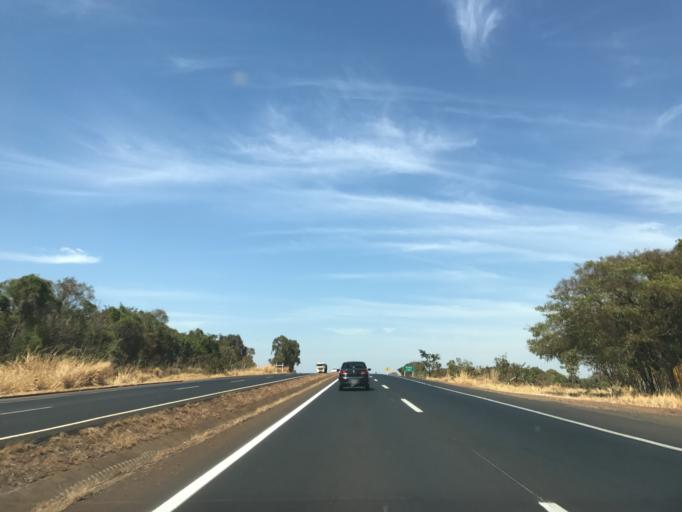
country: BR
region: Minas Gerais
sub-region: Monte Alegre De Minas
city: Monte Alegre de Minas
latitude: -18.8078
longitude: -49.0843
